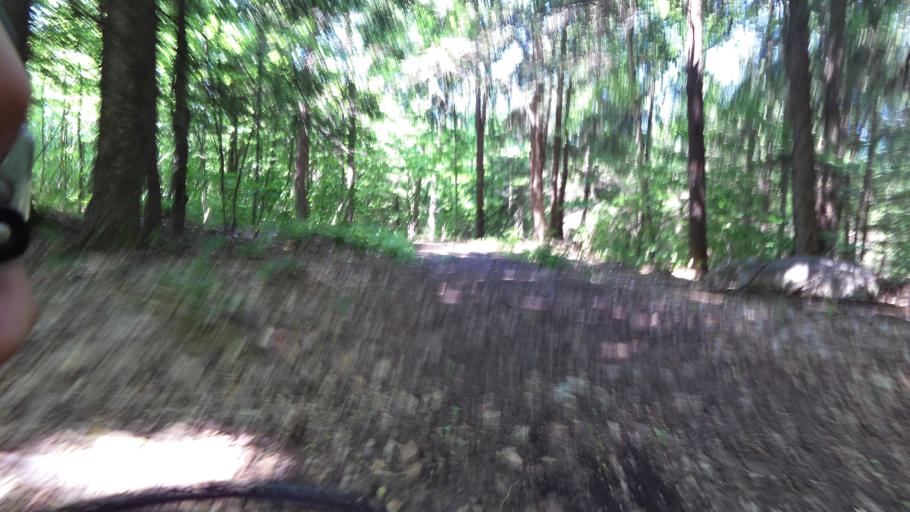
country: CA
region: Quebec
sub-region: Outaouais
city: Wakefield
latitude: 45.5576
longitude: -75.9001
